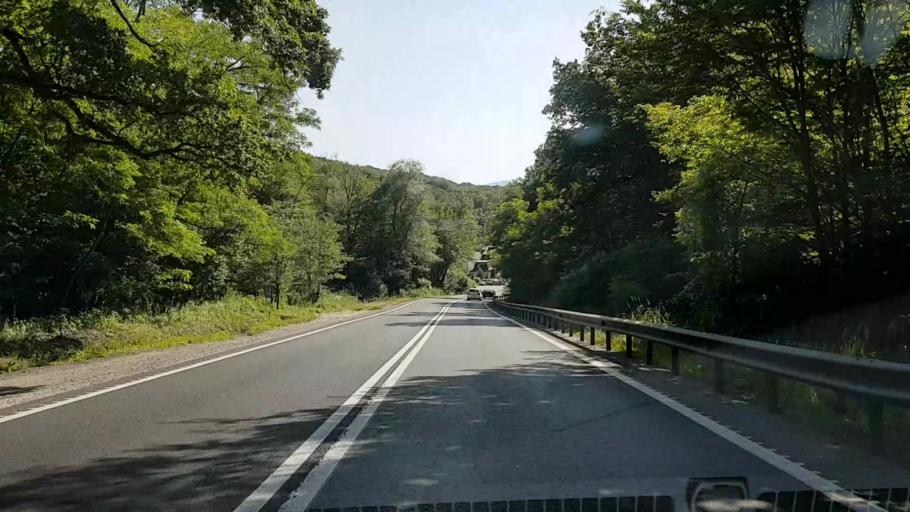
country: RO
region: Sibiu
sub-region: Comuna Talmaciu
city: Talmaciu
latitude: 45.7047
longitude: 24.2897
